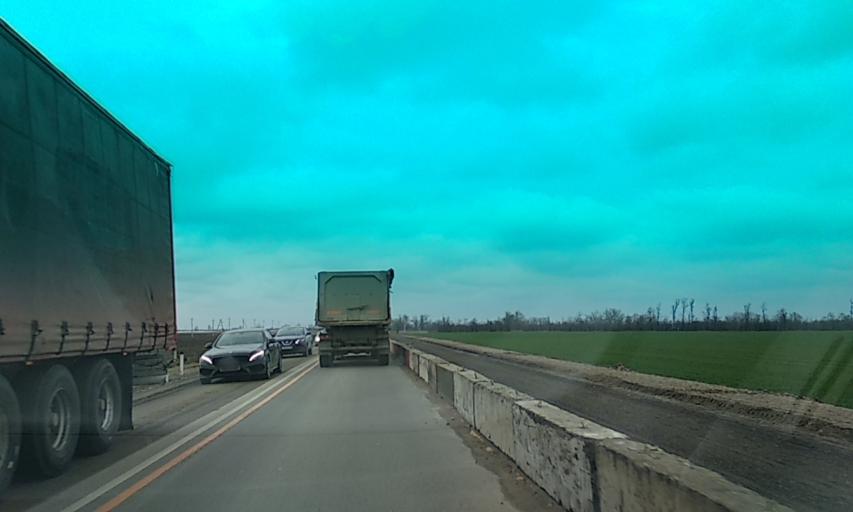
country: RU
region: Adygeya
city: Beloye
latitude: 45.0196
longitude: 39.6908
